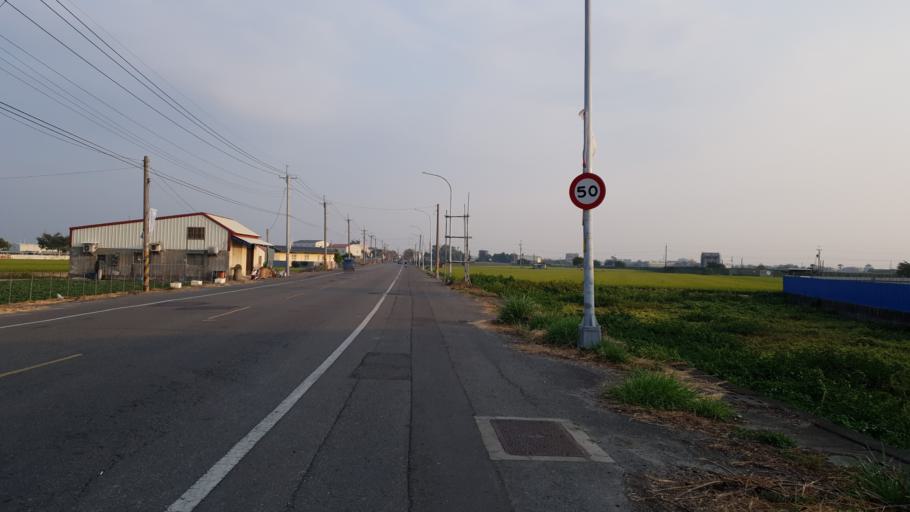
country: TW
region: Taiwan
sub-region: Yunlin
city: Douliu
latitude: 23.7671
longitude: 120.4161
